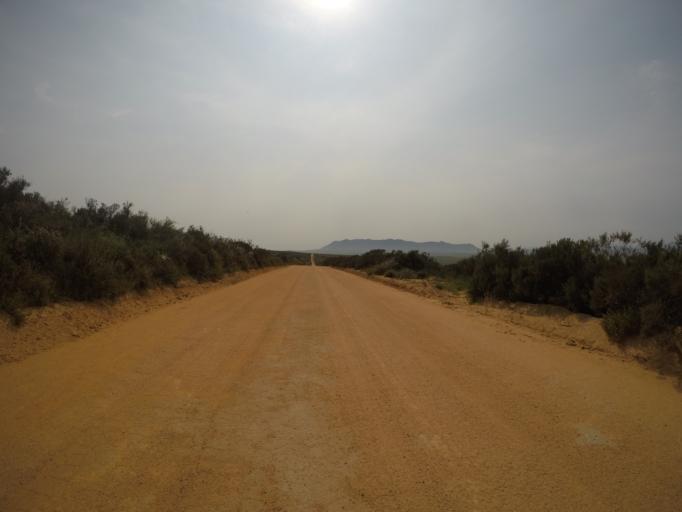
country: ZA
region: Western Cape
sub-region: West Coast District Municipality
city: Malmesbury
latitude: -33.4522
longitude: 18.7440
